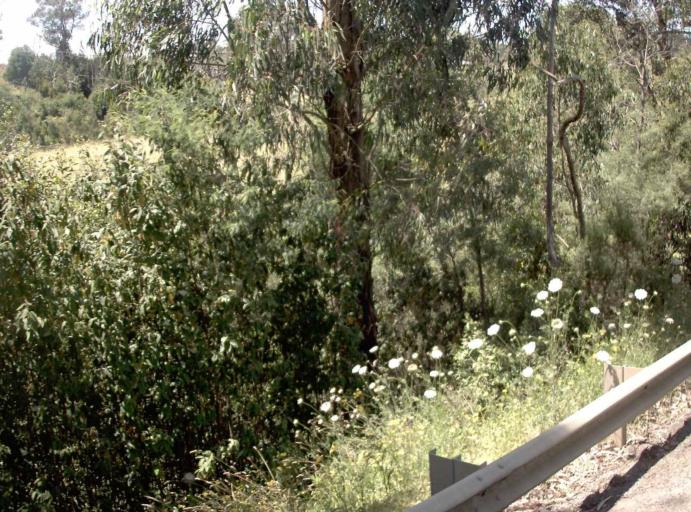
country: AU
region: Victoria
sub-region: Baw Baw
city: Warragul
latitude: -38.0743
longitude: 145.8938
